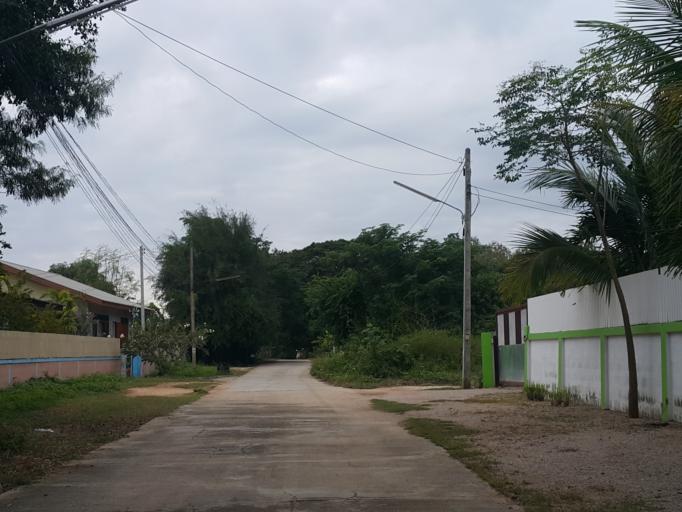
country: TH
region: Lampang
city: Lampang
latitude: 18.3073
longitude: 99.4986
